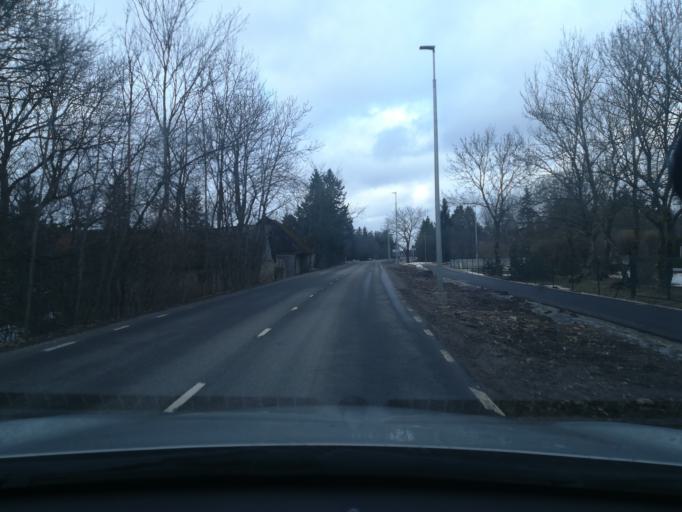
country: EE
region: Harju
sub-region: Harku vald
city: Tabasalu
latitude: 59.4255
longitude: 24.5295
